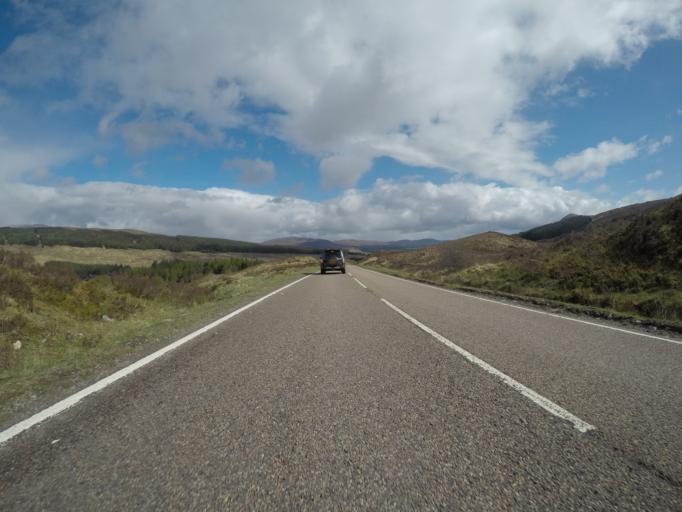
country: GB
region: Scotland
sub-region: Highland
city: Spean Bridge
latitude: 57.1234
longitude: -4.9714
